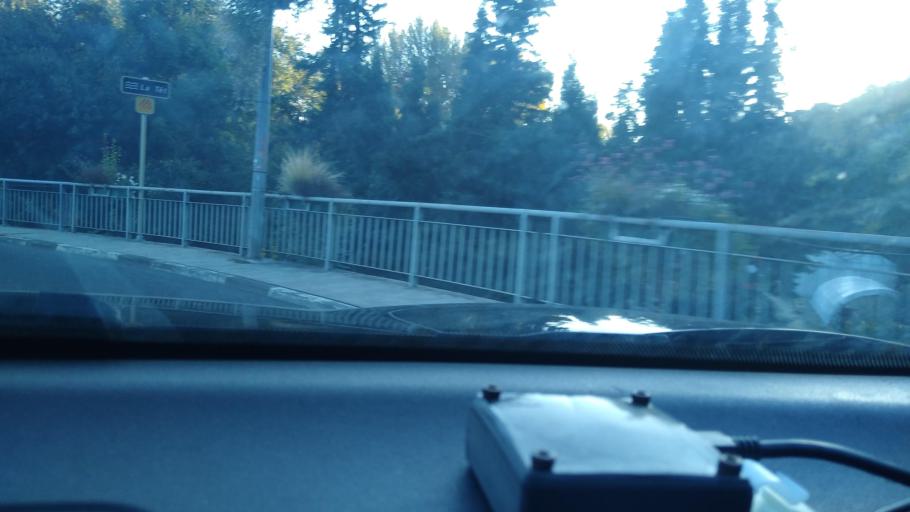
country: FR
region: Languedoc-Roussillon
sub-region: Departement des Pyrenees-Orientales
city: Ria-Sirach
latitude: 42.6212
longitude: 2.4143
